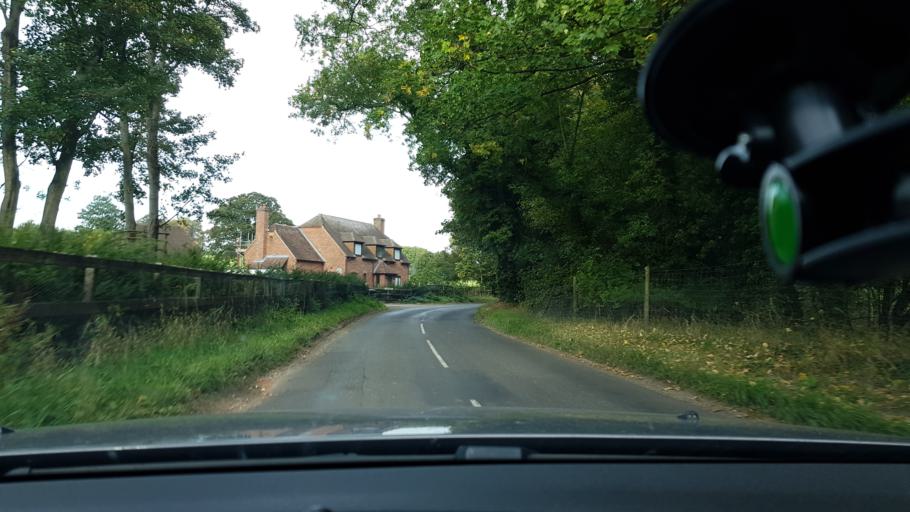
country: GB
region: England
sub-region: West Berkshire
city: Kintbury
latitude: 51.4022
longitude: -1.4686
